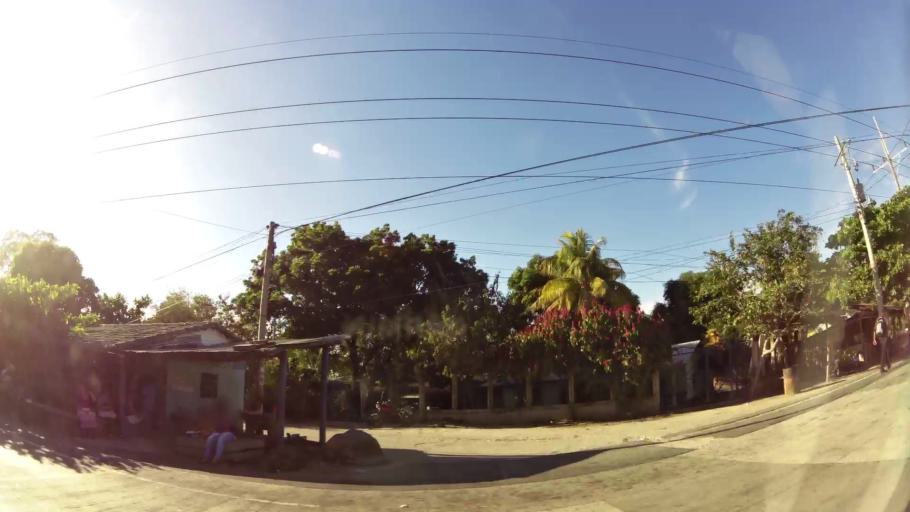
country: SV
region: Santa Ana
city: Metapan
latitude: 14.2439
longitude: -89.4714
